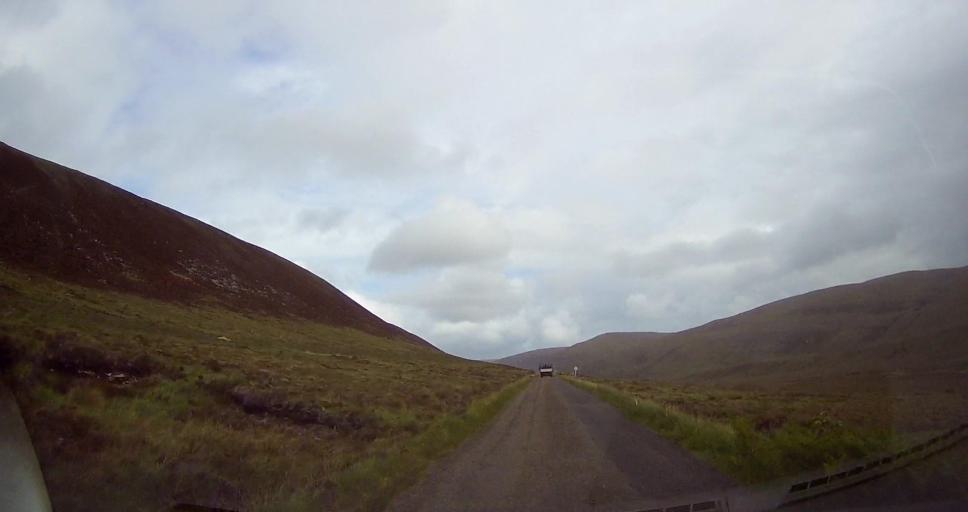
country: GB
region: Scotland
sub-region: Orkney Islands
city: Stromness
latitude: 58.8815
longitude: -3.3681
